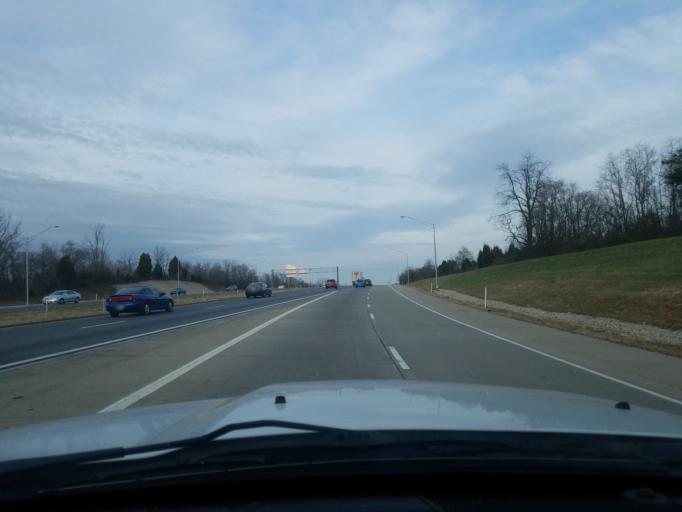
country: US
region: Indiana
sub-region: Floyd County
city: Georgetown
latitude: 38.2898
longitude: -85.9088
